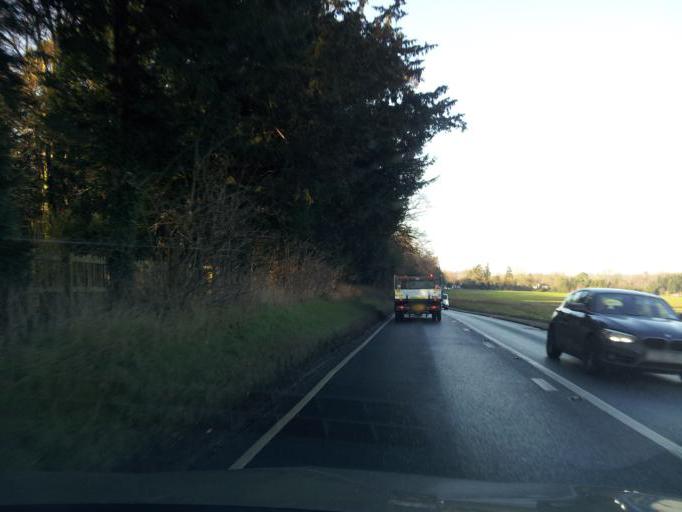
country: GB
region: England
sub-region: Suffolk
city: Bury St Edmunds
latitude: 52.2247
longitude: 0.7353
